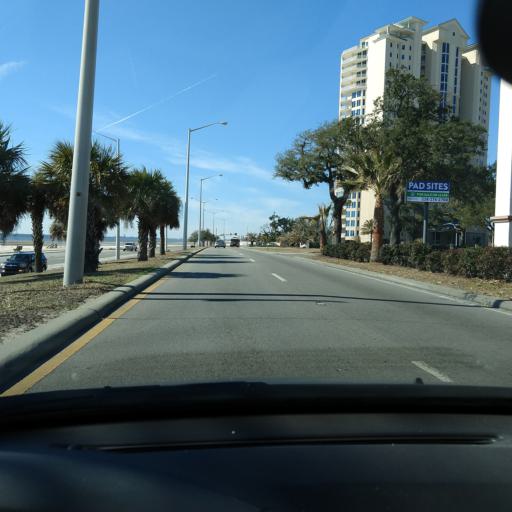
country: US
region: Mississippi
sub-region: Harrison County
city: Gulfport
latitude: 30.3889
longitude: -88.9932
